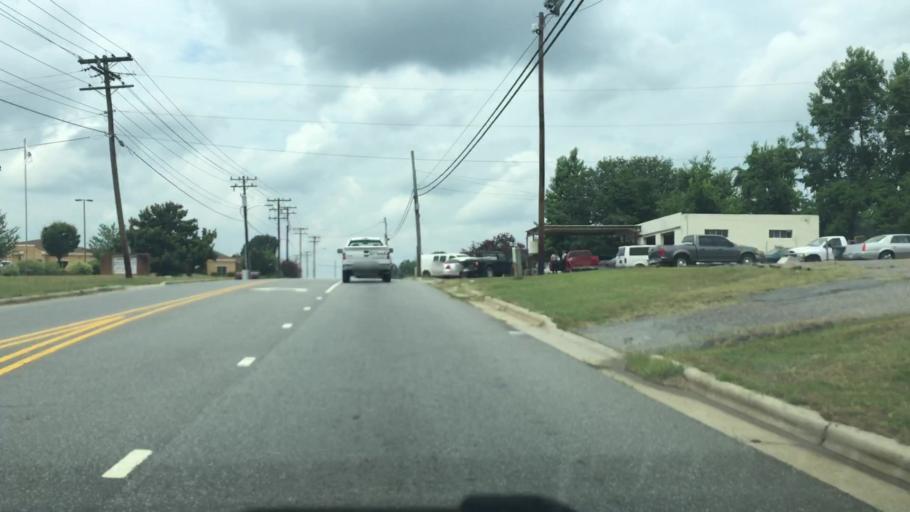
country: US
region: North Carolina
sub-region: Iredell County
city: Troutman
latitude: 35.6994
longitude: -80.8831
